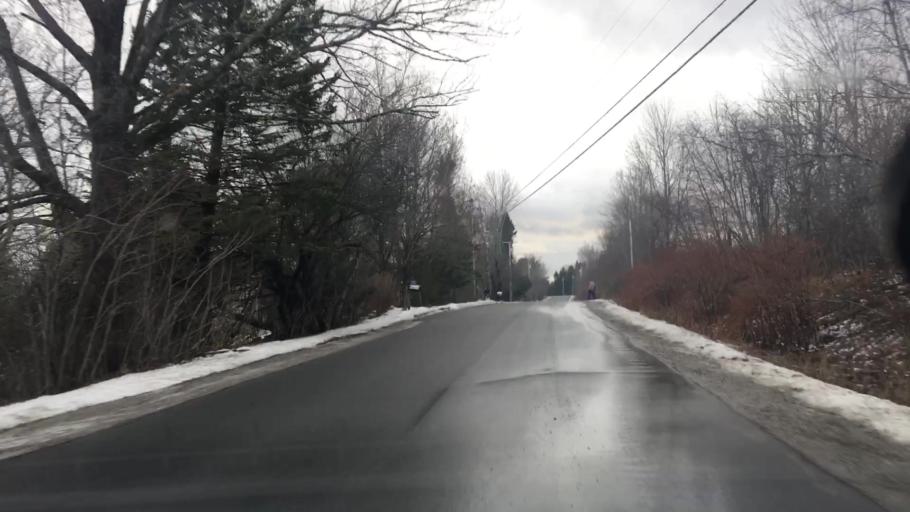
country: US
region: Maine
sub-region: Hancock County
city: Dedham
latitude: 44.6635
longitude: -68.7033
